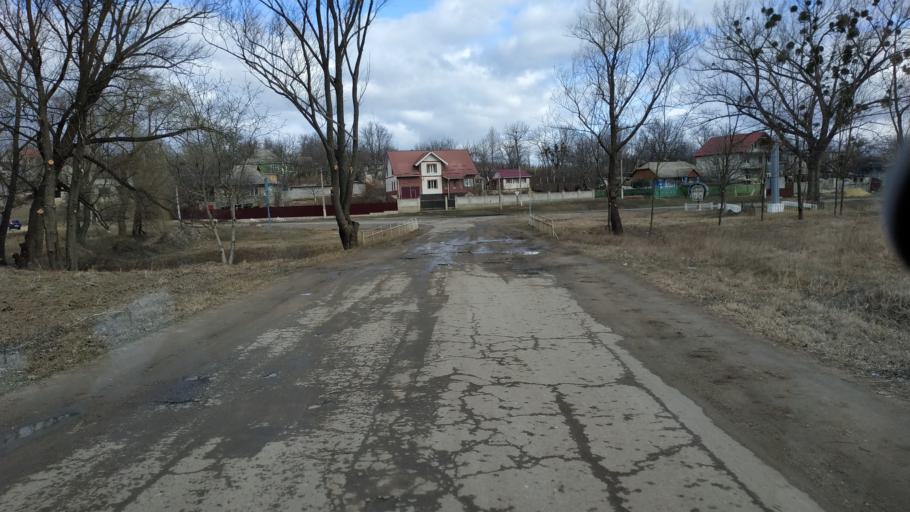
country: MD
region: Calarasi
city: Calarasi
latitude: 47.1318
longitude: 28.3129
